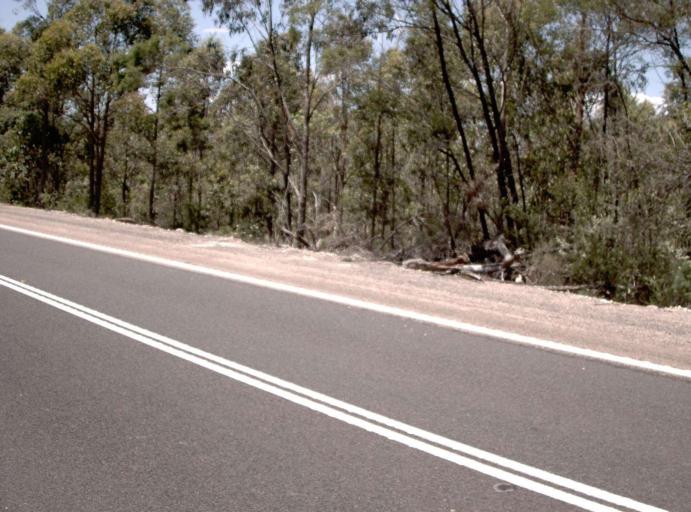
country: AU
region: Victoria
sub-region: East Gippsland
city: Lakes Entrance
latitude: -37.6997
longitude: 148.6089
